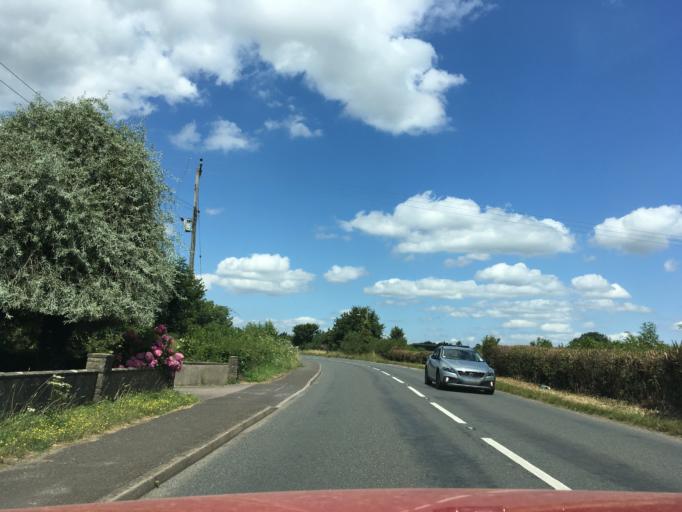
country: GB
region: England
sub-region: South Gloucestershire
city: Falfield
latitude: 51.6096
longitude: -2.4381
